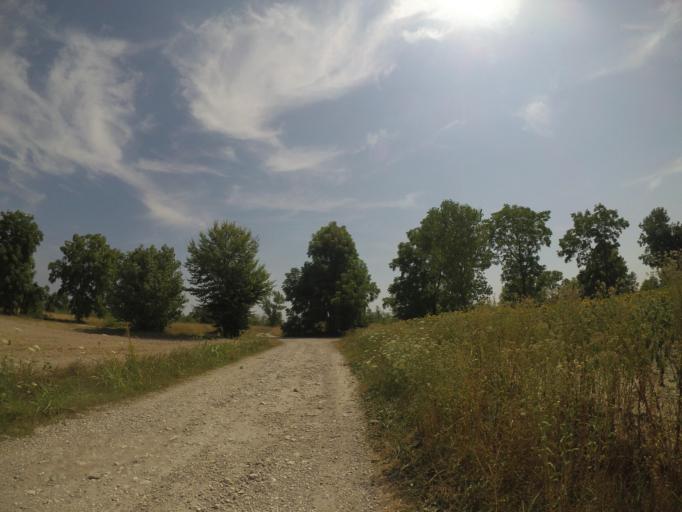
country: IT
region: Friuli Venezia Giulia
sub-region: Provincia di Pordenone
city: Rosa
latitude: 45.9404
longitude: 12.8991
